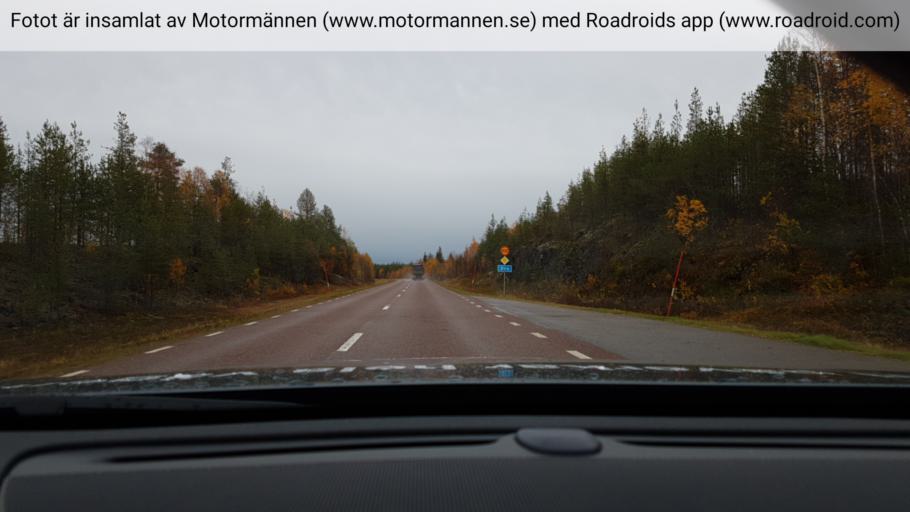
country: SE
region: Norrbotten
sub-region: Pajala Kommun
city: Pajala
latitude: 67.1673
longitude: 22.6564
